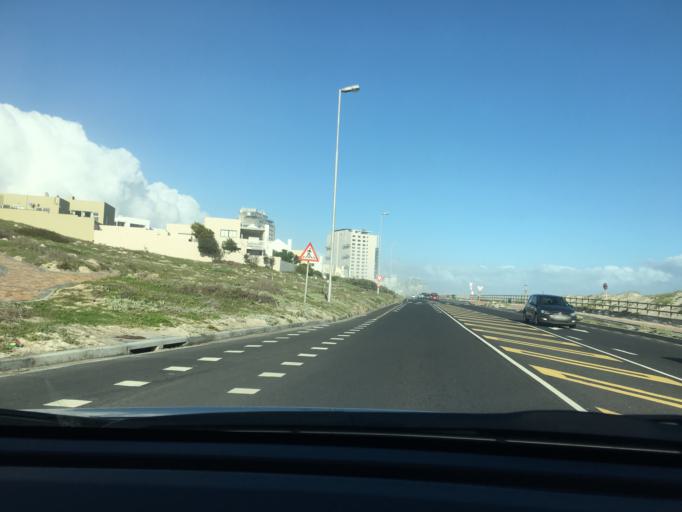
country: ZA
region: Western Cape
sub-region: City of Cape Town
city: Sunset Beach
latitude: -33.8065
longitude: 18.4660
